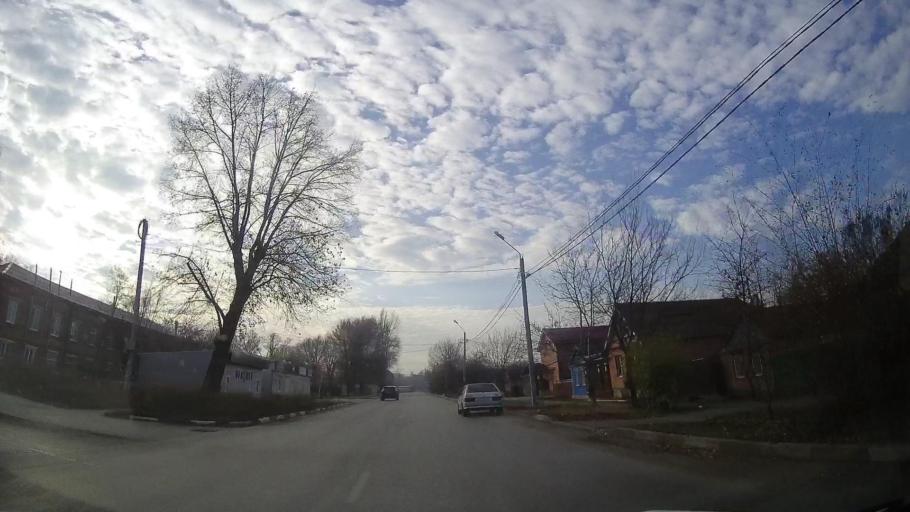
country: RU
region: Rostov
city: Bataysk
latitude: 47.1222
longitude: 39.7654
